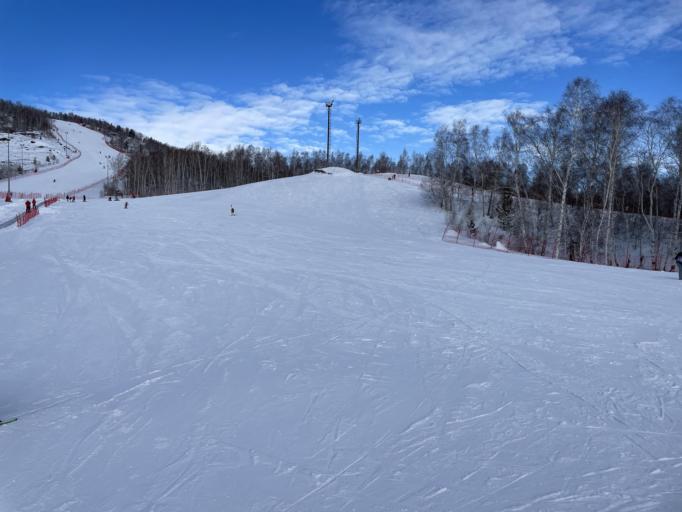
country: RU
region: Bashkortostan
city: Abzakovo
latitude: 53.5910
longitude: 58.5807
